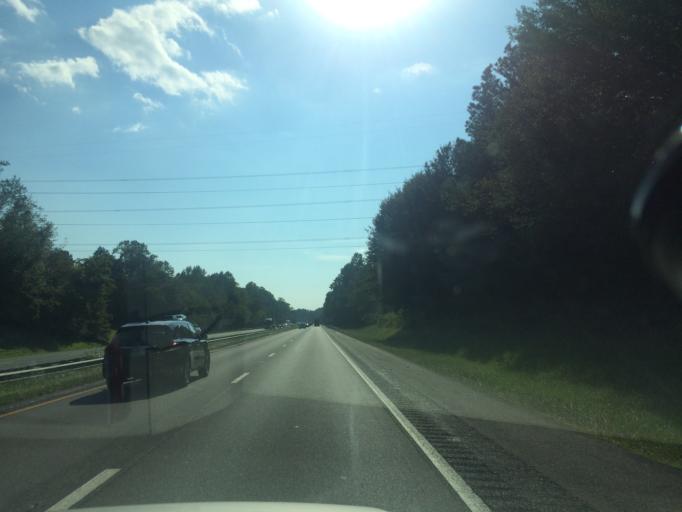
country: US
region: North Carolina
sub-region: Cleveland County
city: White Plains
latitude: 35.1701
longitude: -81.4344
